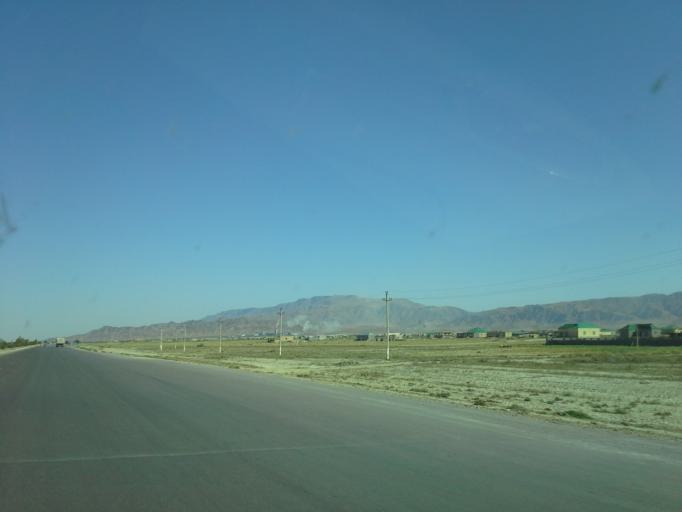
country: TM
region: Ahal
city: Baharly
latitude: 38.3126
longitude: 57.6101
